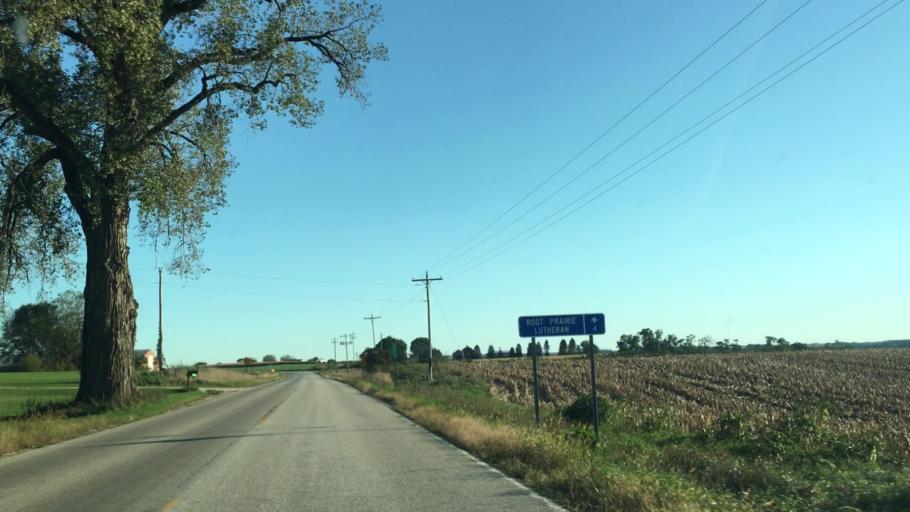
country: US
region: Minnesota
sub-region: Fillmore County
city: Chatfield
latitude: 43.8211
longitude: -92.0690
